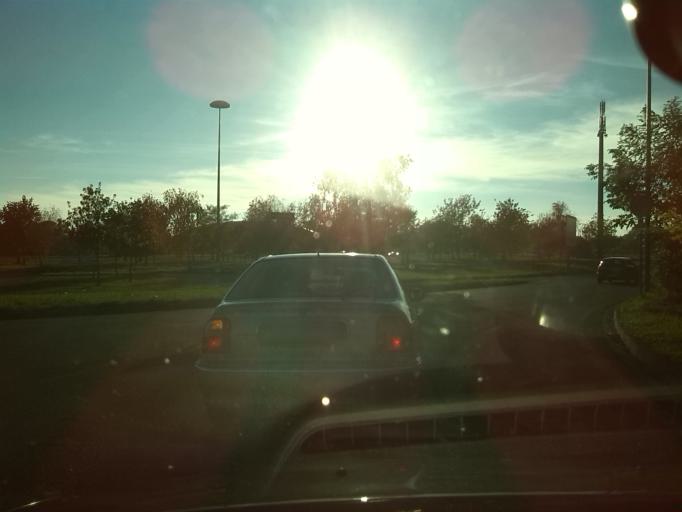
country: IT
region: Friuli Venezia Giulia
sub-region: Provincia di Udine
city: Colugna
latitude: 46.0851
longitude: 13.1972
